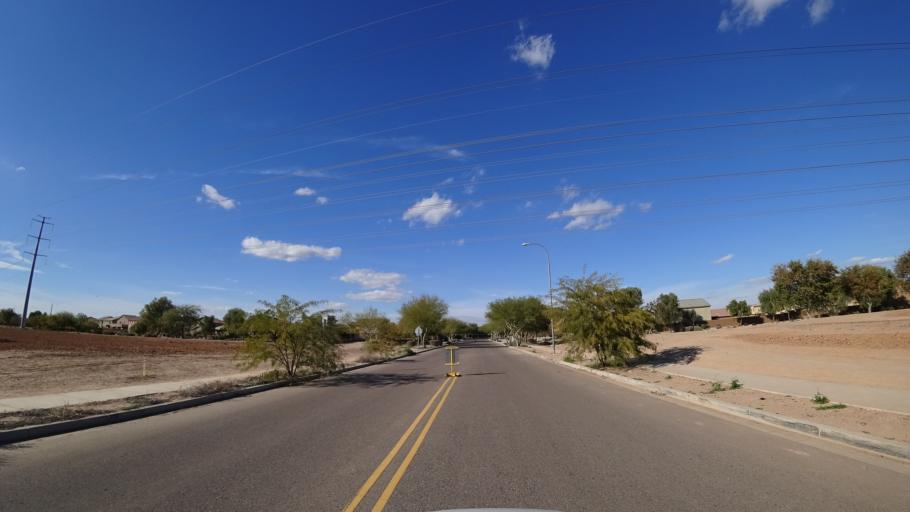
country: US
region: Arizona
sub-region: Maricopa County
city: Tolleson
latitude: 33.4140
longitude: -112.2512
